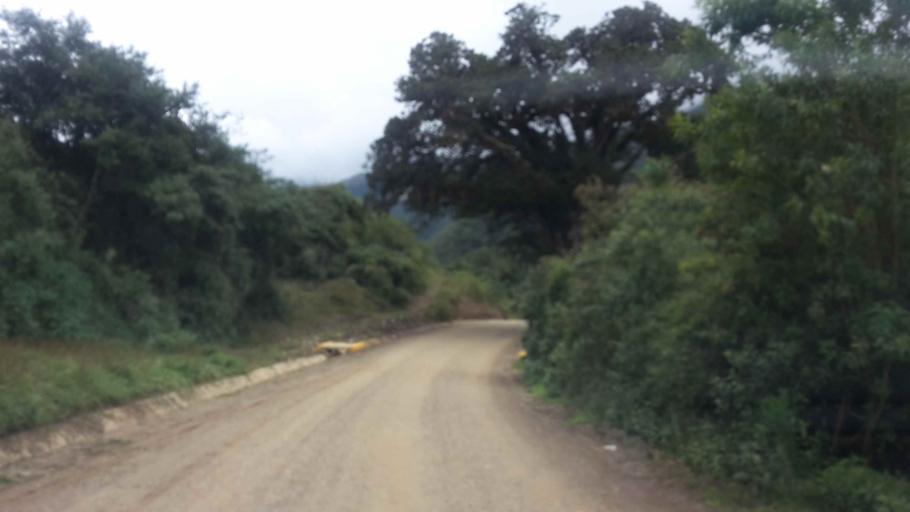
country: BO
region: Cochabamba
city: Totora
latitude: -17.5695
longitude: -65.2805
